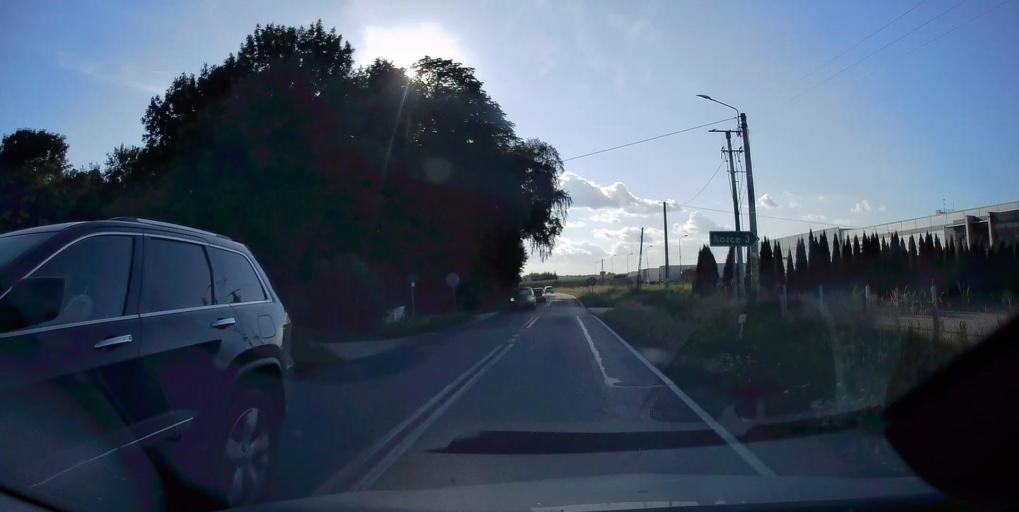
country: PL
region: Masovian Voivodeship
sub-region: Powiat grojecki
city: Bledow
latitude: 51.8144
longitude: 20.7418
